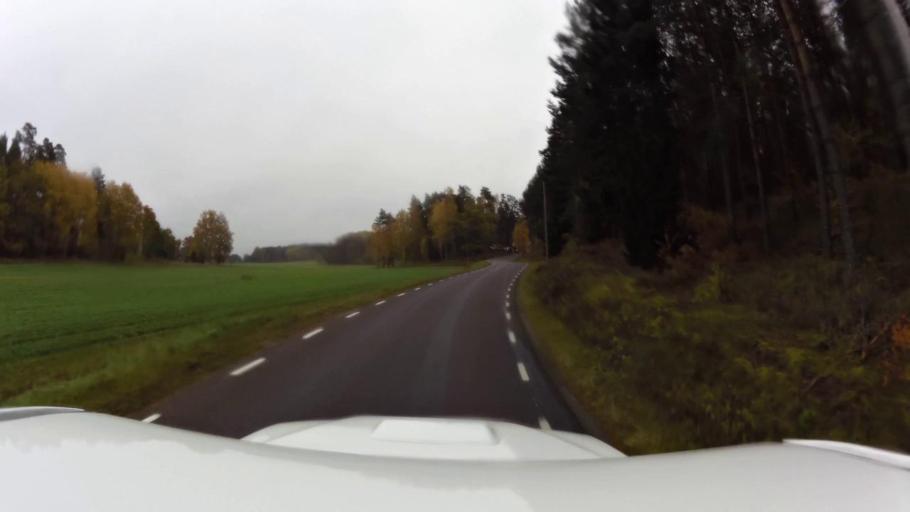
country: SE
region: OEstergoetland
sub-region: Linkopings Kommun
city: Linghem
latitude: 58.3576
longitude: 15.8458
